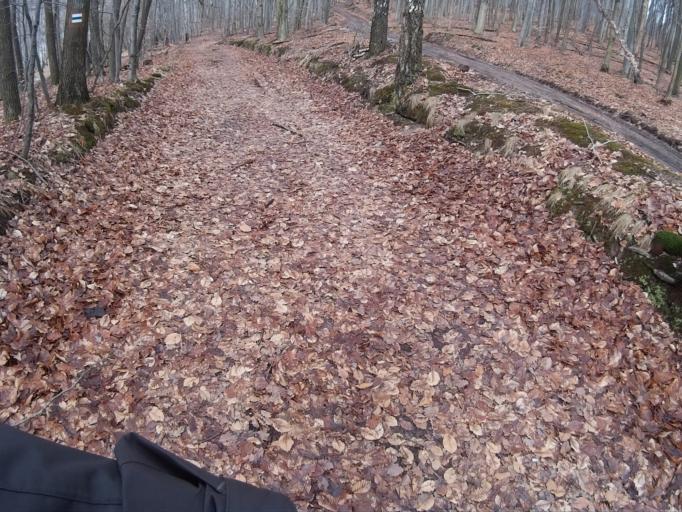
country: HU
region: Borsod-Abauj-Zemplen
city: Tolcsva
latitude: 48.4071
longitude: 21.4045
